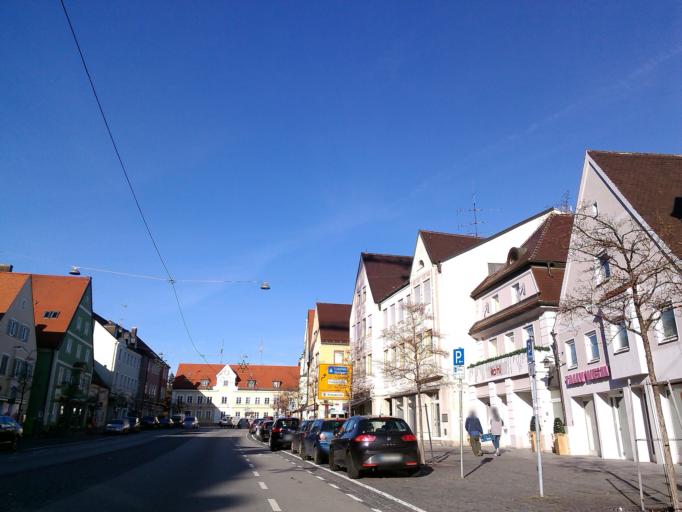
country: DE
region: Bavaria
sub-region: Upper Bavaria
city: Fuerstenfeldbruck
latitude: 48.1783
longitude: 11.2551
